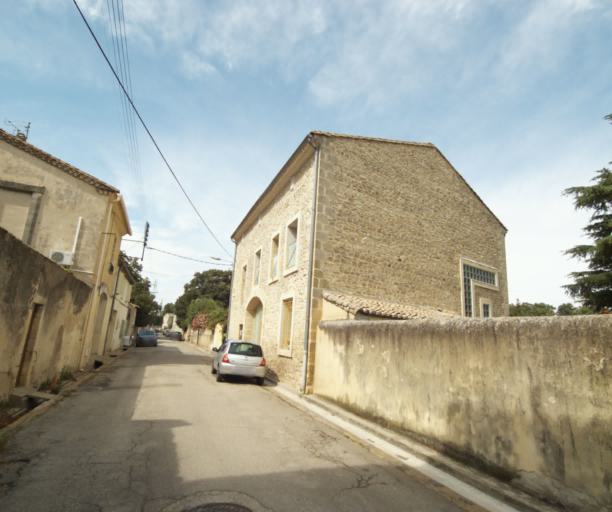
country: FR
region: Languedoc-Roussillon
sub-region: Departement de l'Herault
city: Marsillargues
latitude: 43.6646
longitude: 4.1818
